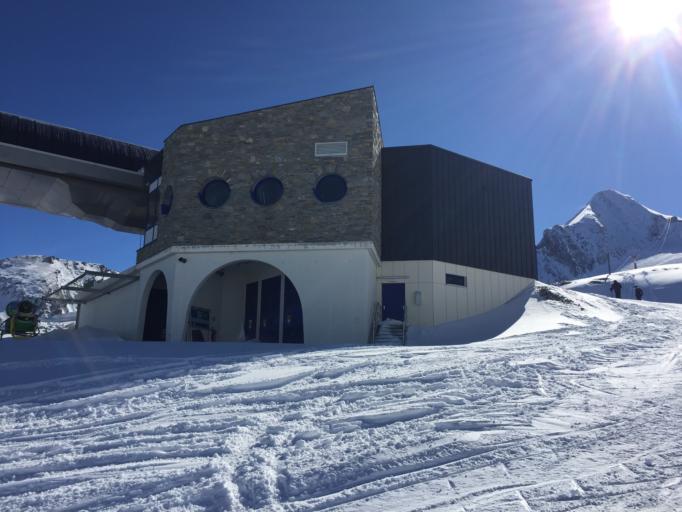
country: AT
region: Salzburg
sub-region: Politischer Bezirk Zell am See
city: Piesendorf
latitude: 47.2095
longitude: 12.6893
